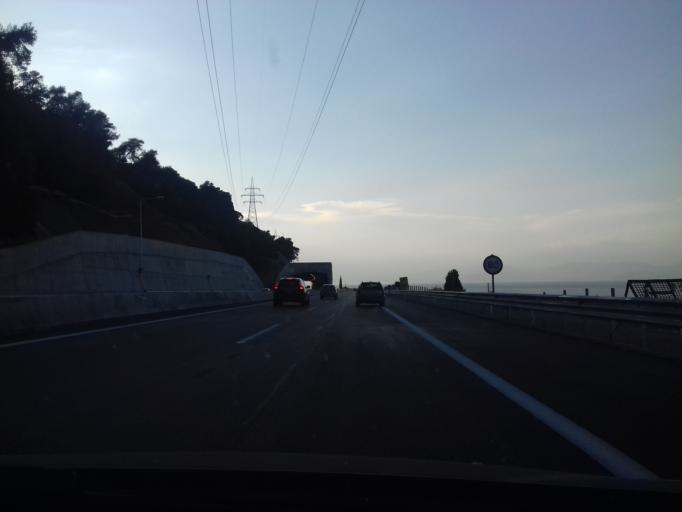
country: GR
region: West Greece
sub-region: Nomos Achaias
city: Aiyira
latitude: 38.1284
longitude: 22.4492
